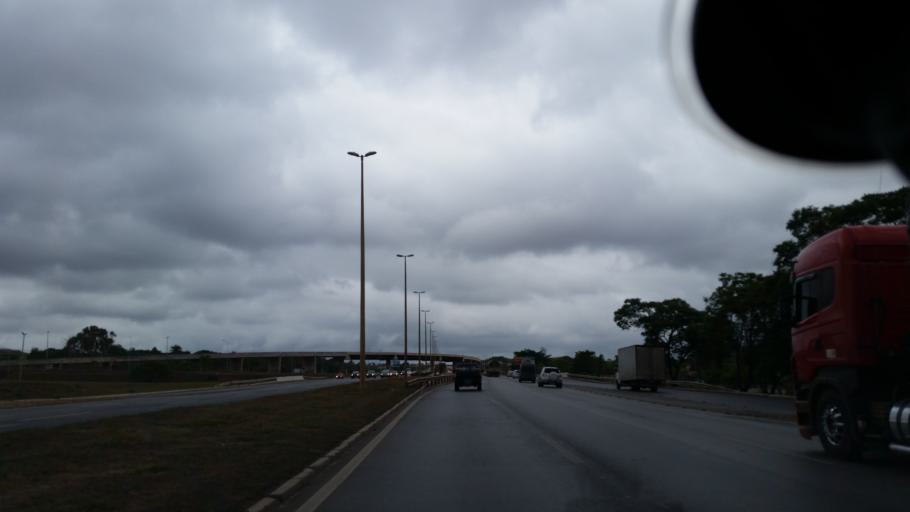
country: BR
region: Federal District
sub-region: Brasilia
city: Brasilia
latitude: -15.8733
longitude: -47.9586
